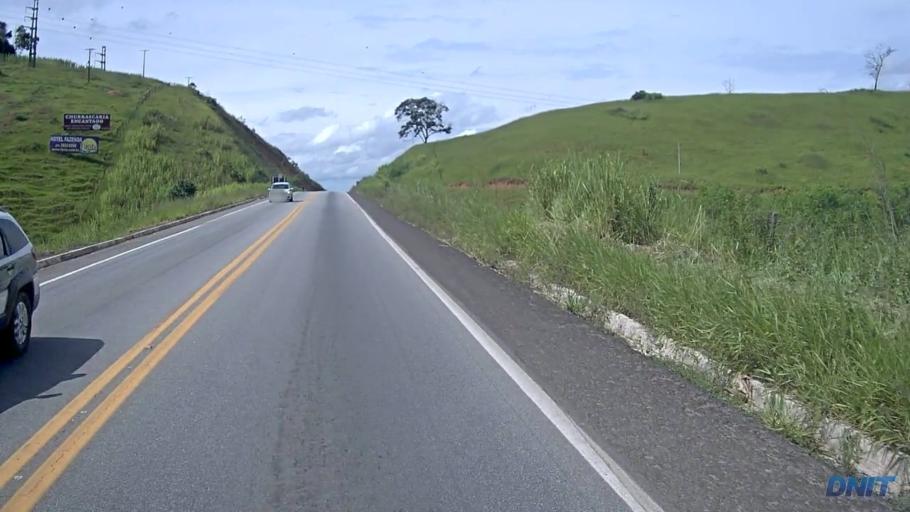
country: BR
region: Minas Gerais
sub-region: Ipatinga
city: Ipatinga
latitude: -19.4169
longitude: -42.4926
